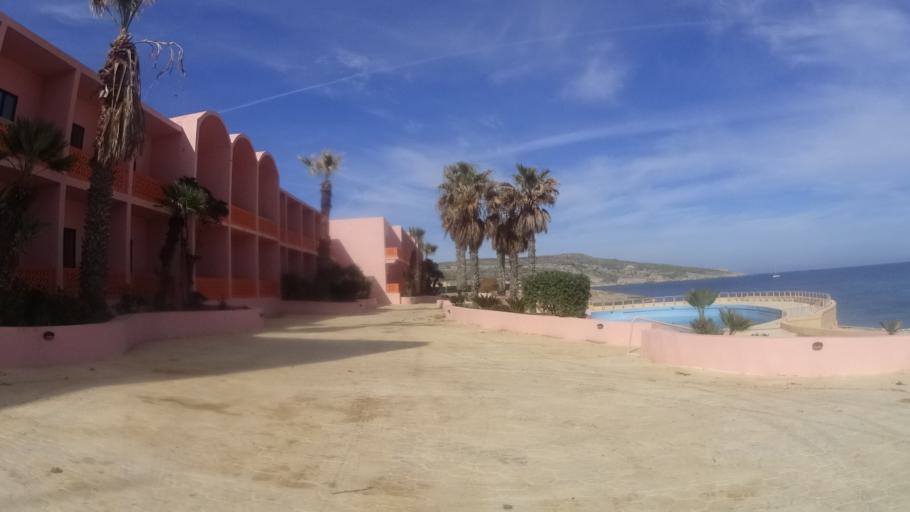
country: MT
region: Il-Qala
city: Qala
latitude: 36.0172
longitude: 14.3286
